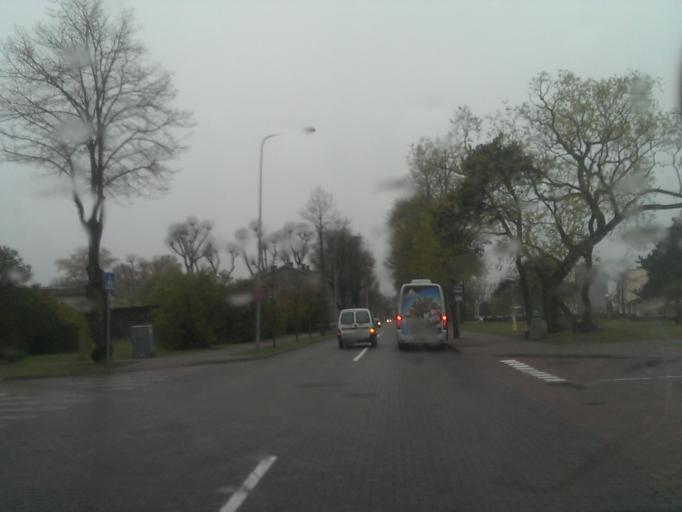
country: LV
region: Ventspils
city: Ventspils
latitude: 57.3921
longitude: 21.5555
